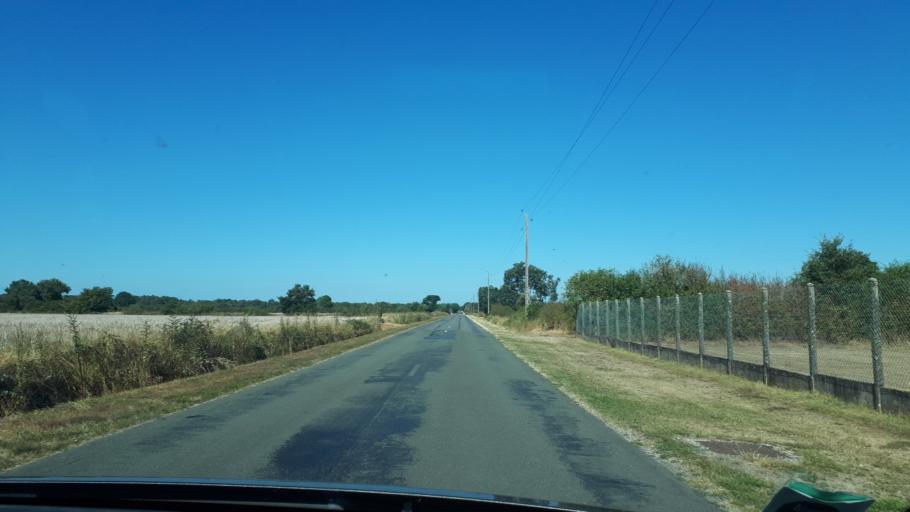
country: FR
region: Centre
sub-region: Departement du Loiret
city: Coullons
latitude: 47.6268
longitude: 2.4844
